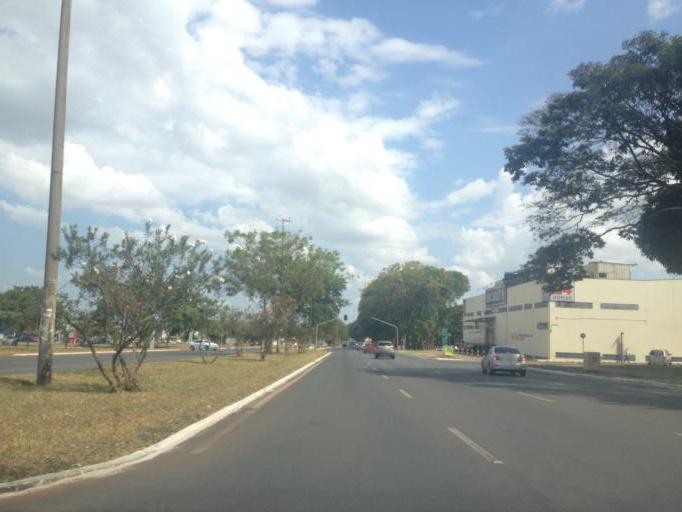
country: BR
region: Federal District
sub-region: Brasilia
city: Brasilia
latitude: -15.8316
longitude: -47.9100
